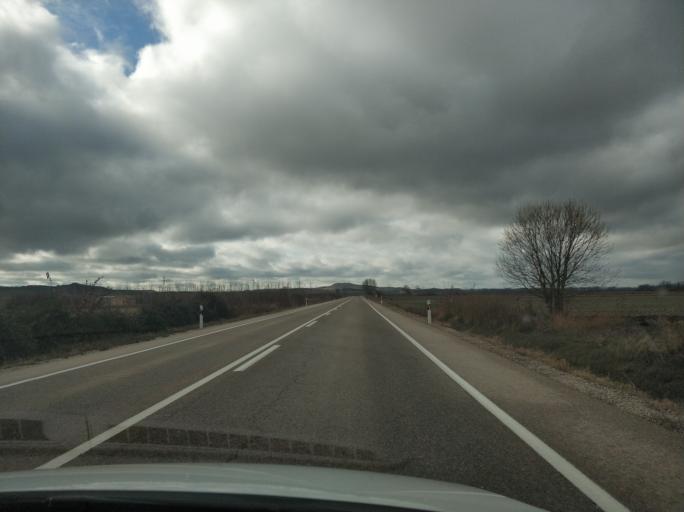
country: ES
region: Castille and Leon
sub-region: Provincia de Soria
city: San Esteban de Gormaz
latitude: 41.5681
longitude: -3.2249
